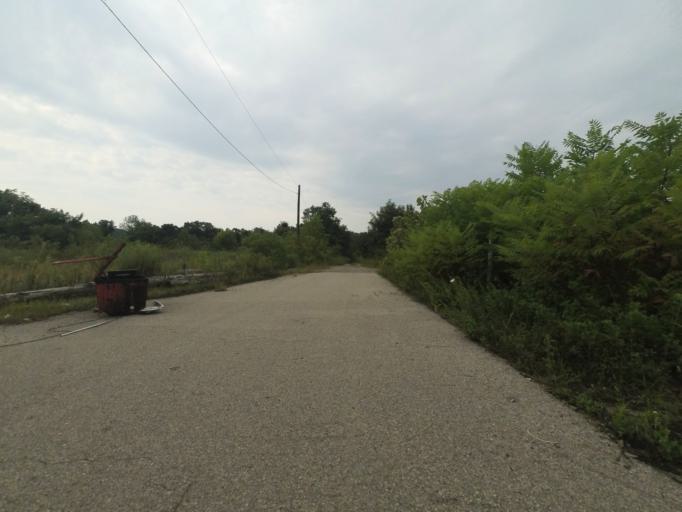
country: US
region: West Virginia
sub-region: Cabell County
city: Huntington
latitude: 38.4287
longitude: -82.4205
